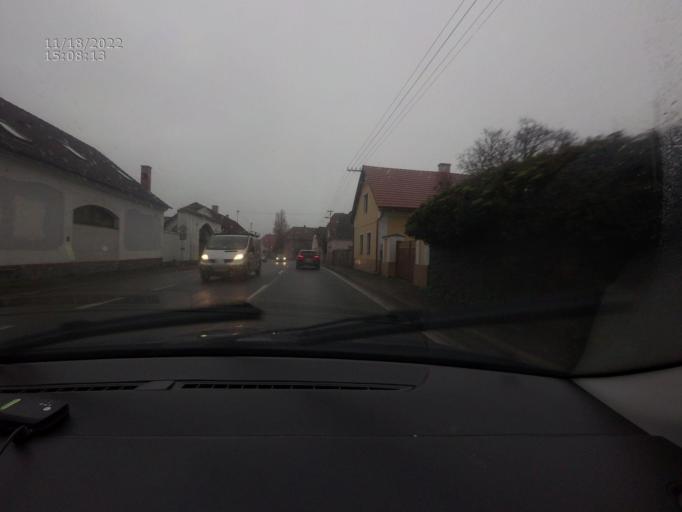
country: CZ
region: Jihocesky
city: Mirovice
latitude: 49.5168
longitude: 14.0891
